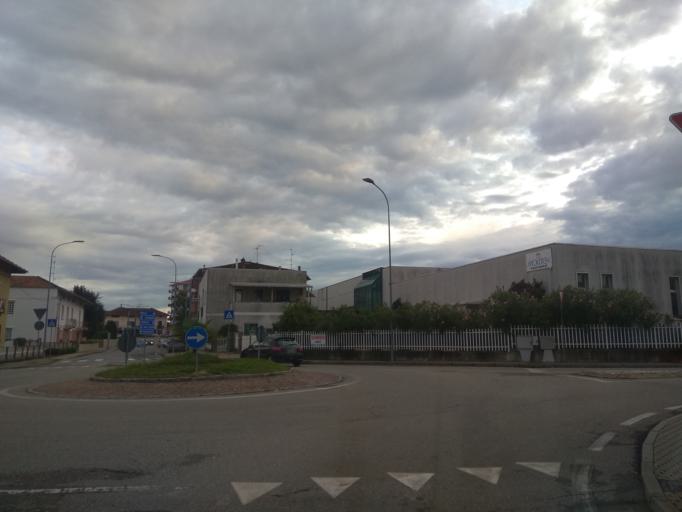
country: IT
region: Piedmont
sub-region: Provincia di Biella
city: Cerreto Castello
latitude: 45.5670
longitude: 8.1674
